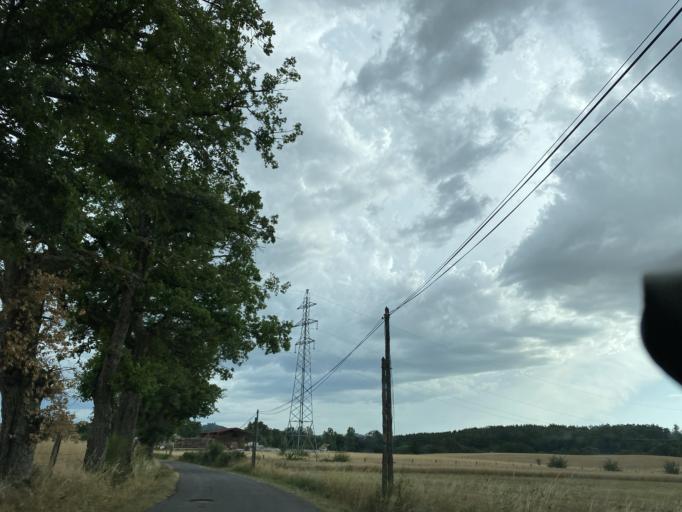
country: FR
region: Auvergne
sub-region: Departement du Puy-de-Dome
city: Courpiere
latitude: 45.7444
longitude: 3.4549
